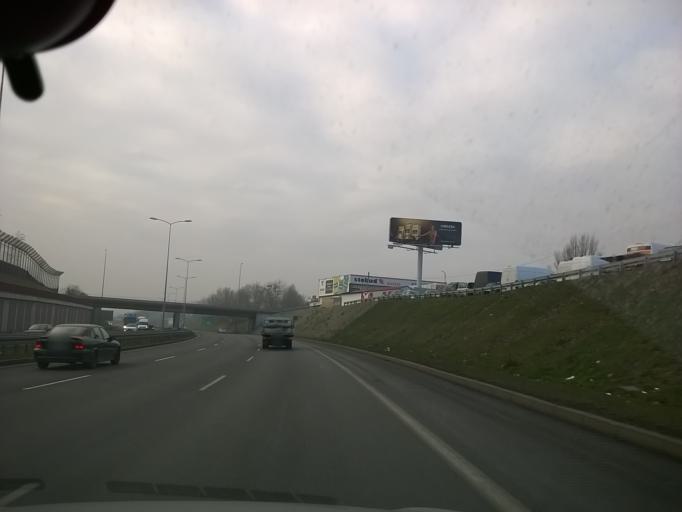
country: PL
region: Silesian Voivodeship
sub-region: Swietochlowice
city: Swietochlowice
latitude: 50.3005
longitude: 18.8779
